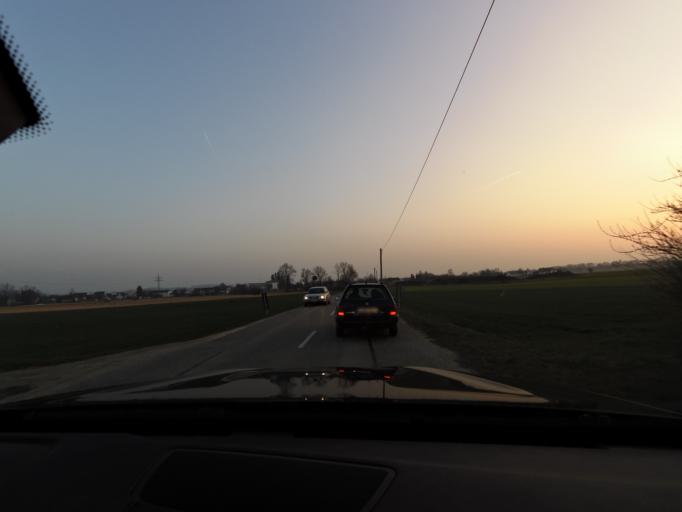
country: DE
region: Bavaria
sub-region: Lower Bavaria
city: Tiefenbach
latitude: 48.5393
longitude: 12.0859
